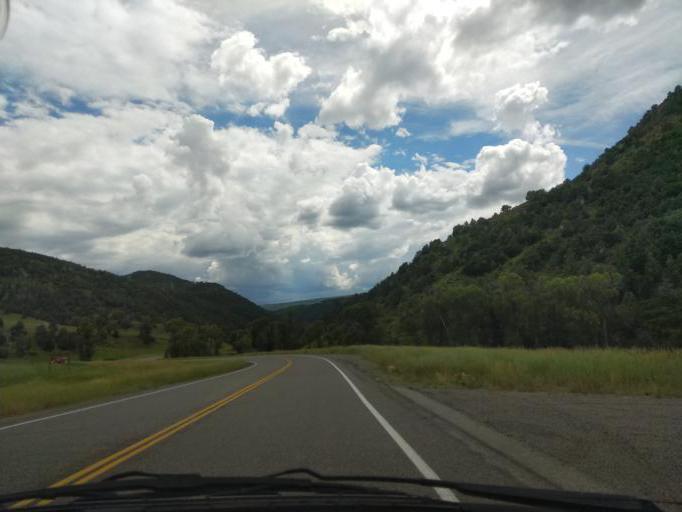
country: US
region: Colorado
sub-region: Delta County
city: Paonia
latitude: 39.0478
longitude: -107.3603
